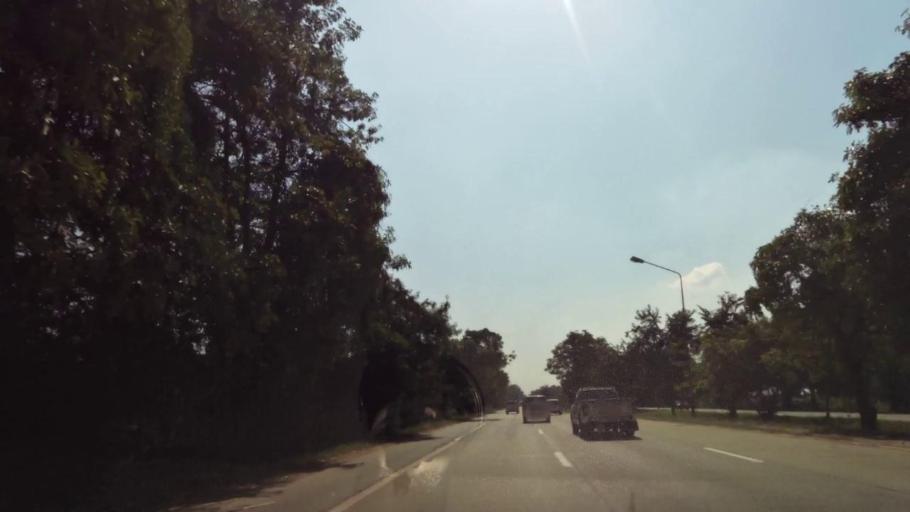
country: TH
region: Phichit
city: Wachira Barami
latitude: 16.5721
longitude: 100.1485
